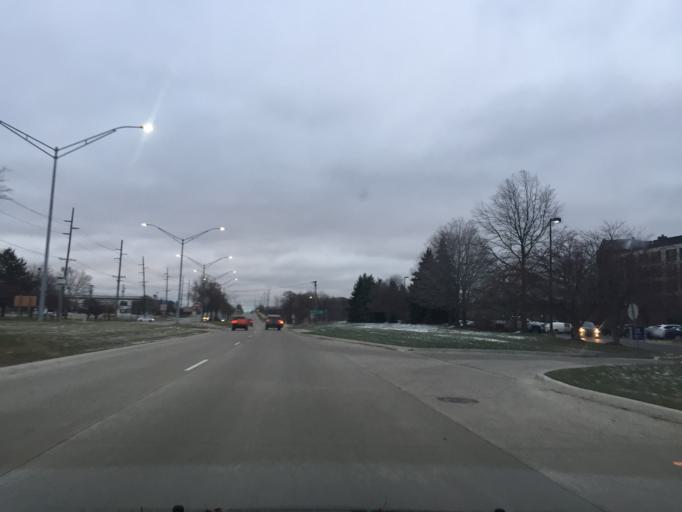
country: US
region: Michigan
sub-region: Oakland County
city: Auburn Hills
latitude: 42.6492
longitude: -83.2455
